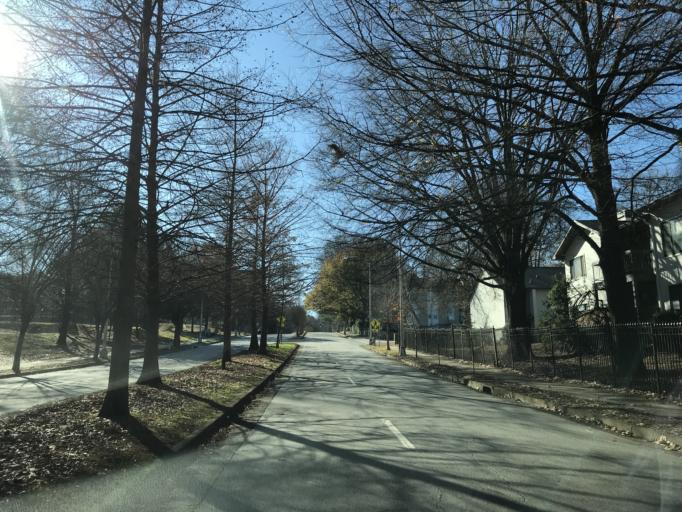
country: US
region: Georgia
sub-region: Fulton County
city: Atlanta
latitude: 33.7693
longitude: -84.3779
